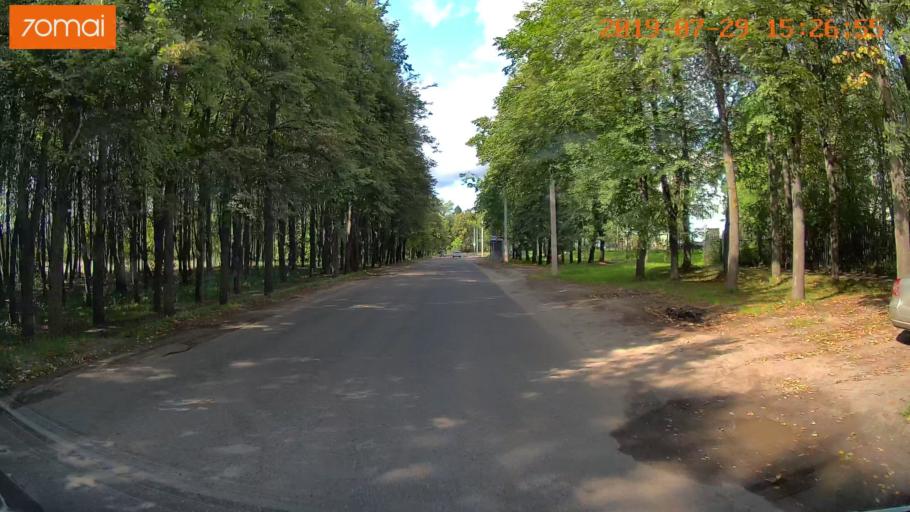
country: RU
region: Ivanovo
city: Bogorodskoye
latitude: 57.0187
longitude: 41.0057
